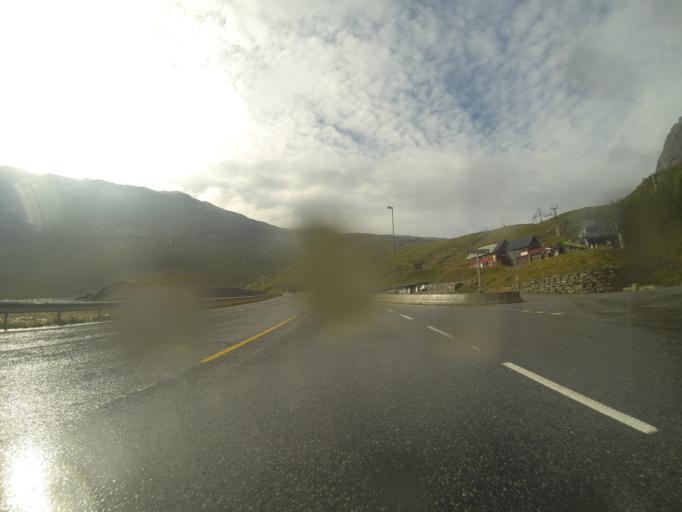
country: NO
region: Hordaland
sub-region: Odda
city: Odda
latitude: 59.8225
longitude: 6.7413
